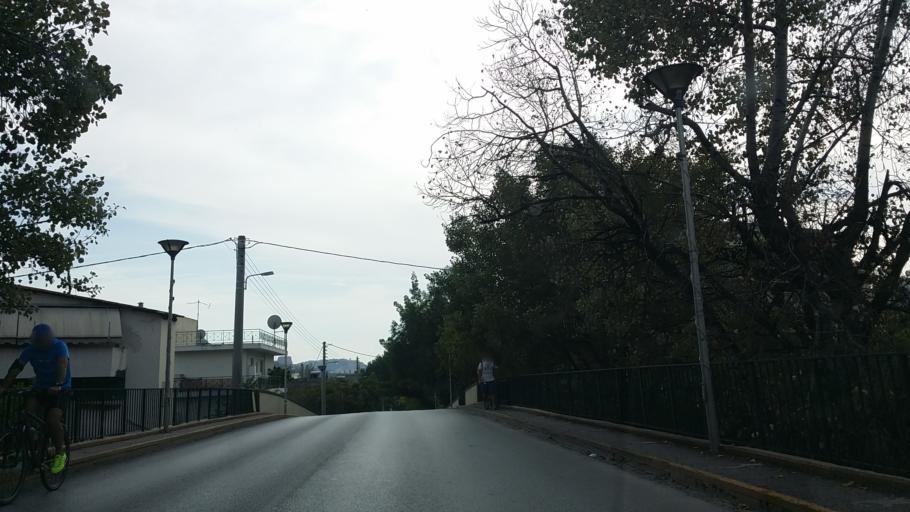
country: GR
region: Attica
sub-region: Nomarchia Athinas
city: Irakleio
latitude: 38.0451
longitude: 23.7731
